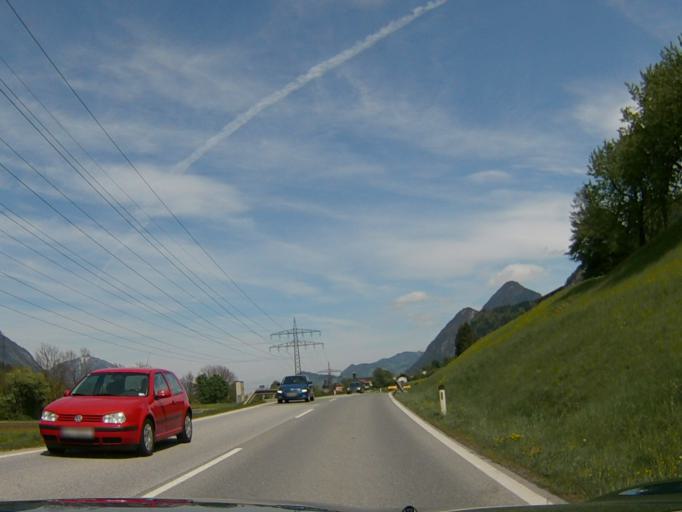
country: AT
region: Tyrol
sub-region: Politischer Bezirk Schwaz
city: Jenbach
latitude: 47.3870
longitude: 11.7876
